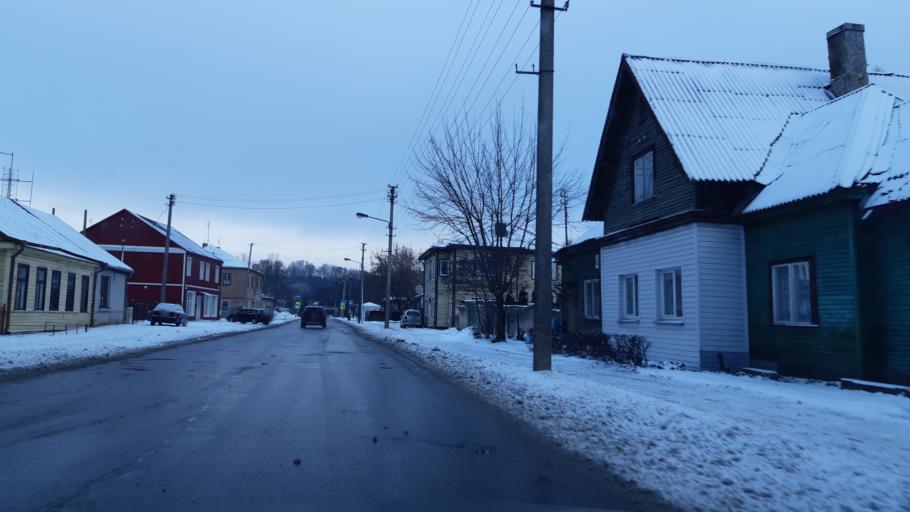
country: LT
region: Kauno apskritis
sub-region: Kaunas
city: Kaunas
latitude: 54.9100
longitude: 23.8889
